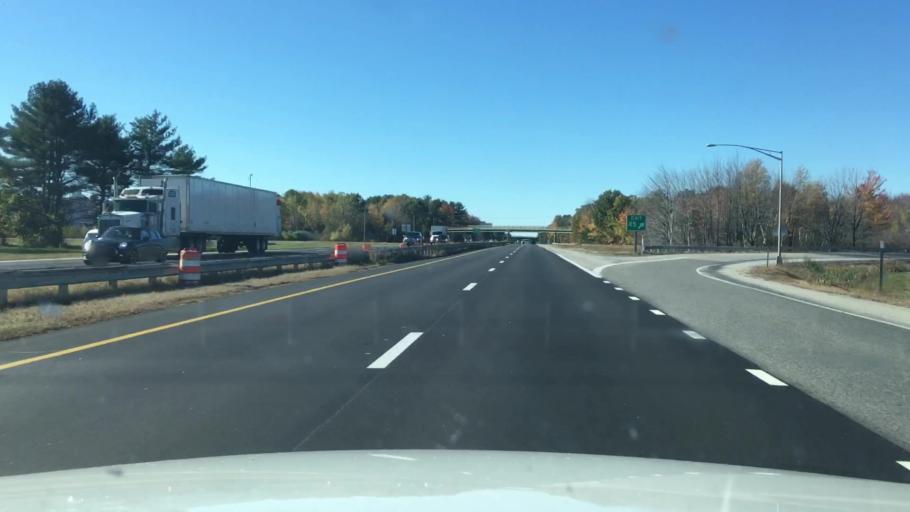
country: US
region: Maine
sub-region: Cumberland County
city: South Portland Gardens
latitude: 43.6314
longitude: -70.3451
